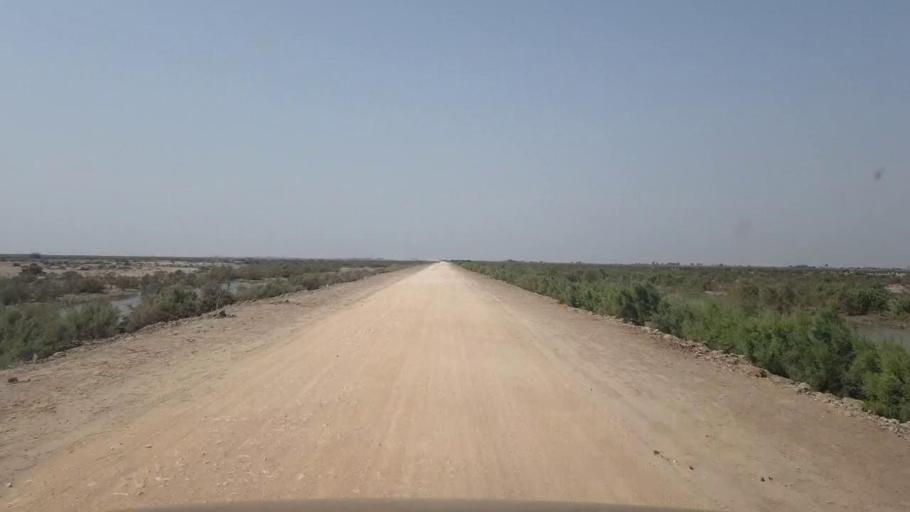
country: PK
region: Sindh
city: Jati
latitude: 24.3810
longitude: 68.5852
